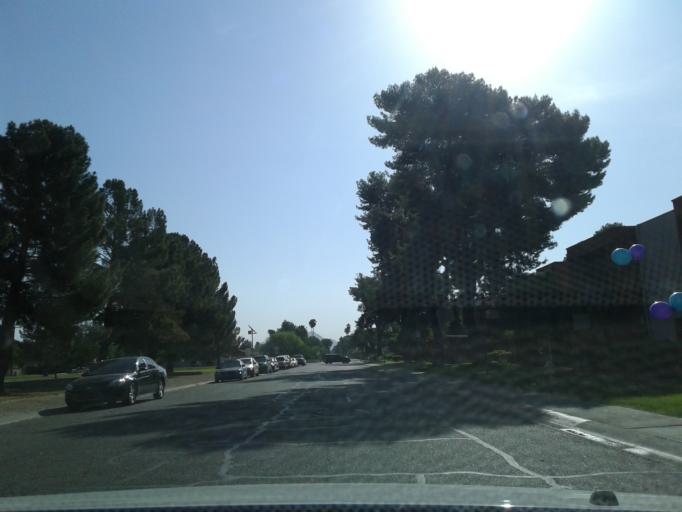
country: US
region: Arizona
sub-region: Maricopa County
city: Phoenix
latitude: 33.5130
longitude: -112.0844
